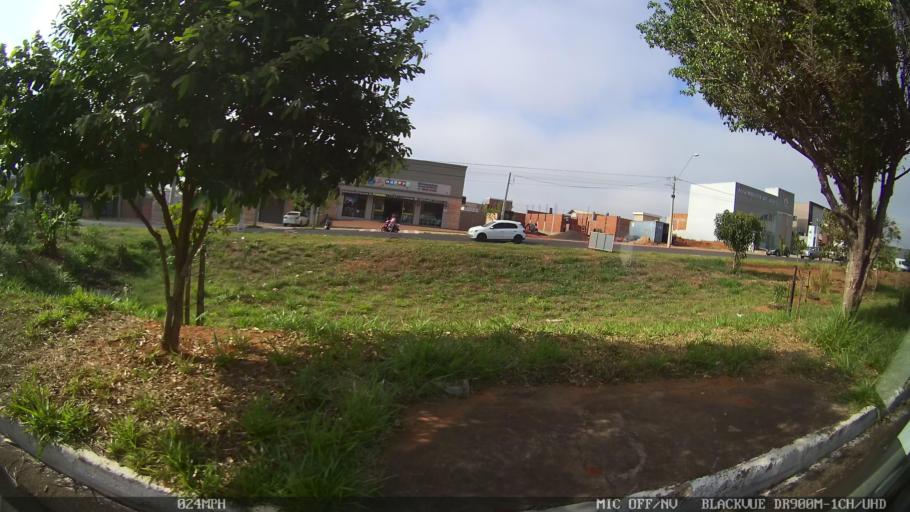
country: BR
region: Sao Paulo
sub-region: Sao Jose Do Rio Preto
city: Sao Jose do Rio Preto
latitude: -20.7981
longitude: -49.4292
